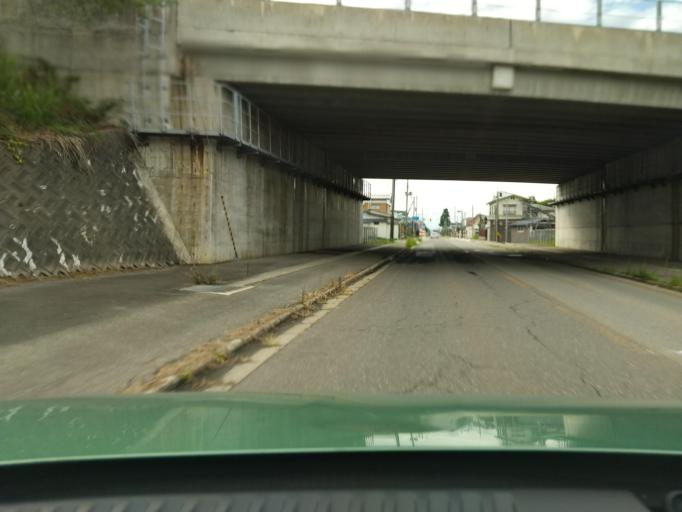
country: JP
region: Akita
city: Yuzawa
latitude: 39.2293
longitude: 140.5179
